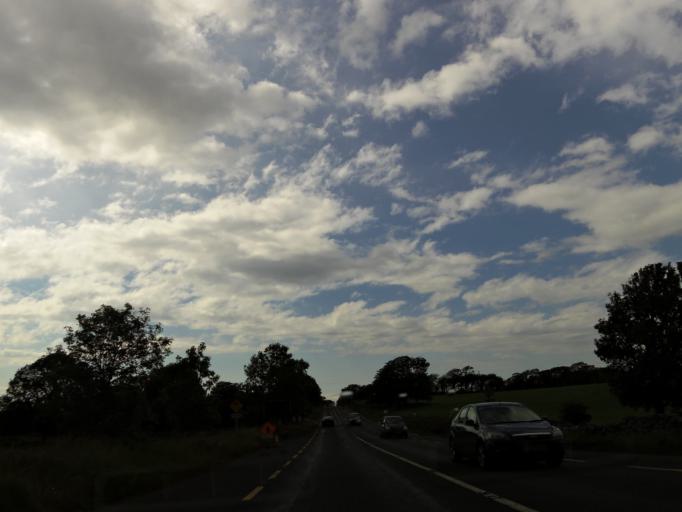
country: IE
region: Connaught
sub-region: County Galway
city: Oranmore
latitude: 53.2553
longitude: -8.9118
